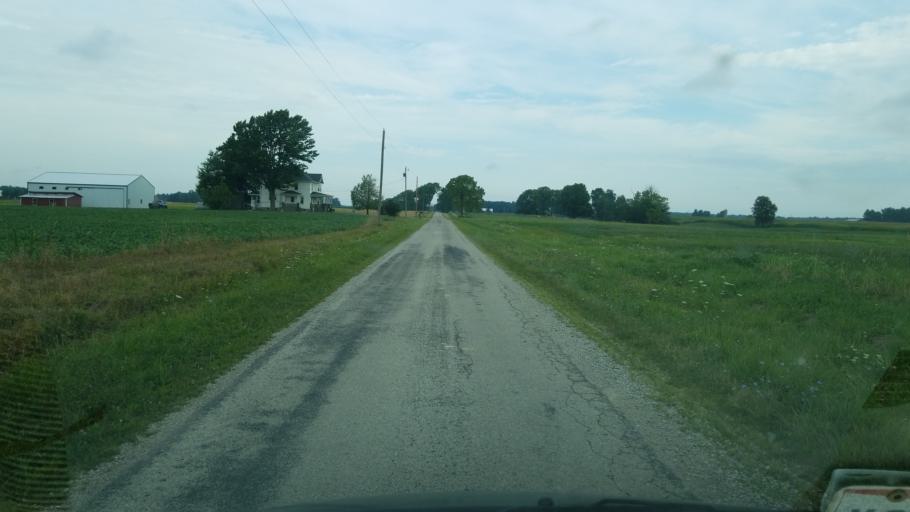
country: US
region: Ohio
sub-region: Seneca County
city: Tiffin
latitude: 40.9838
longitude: -83.0551
